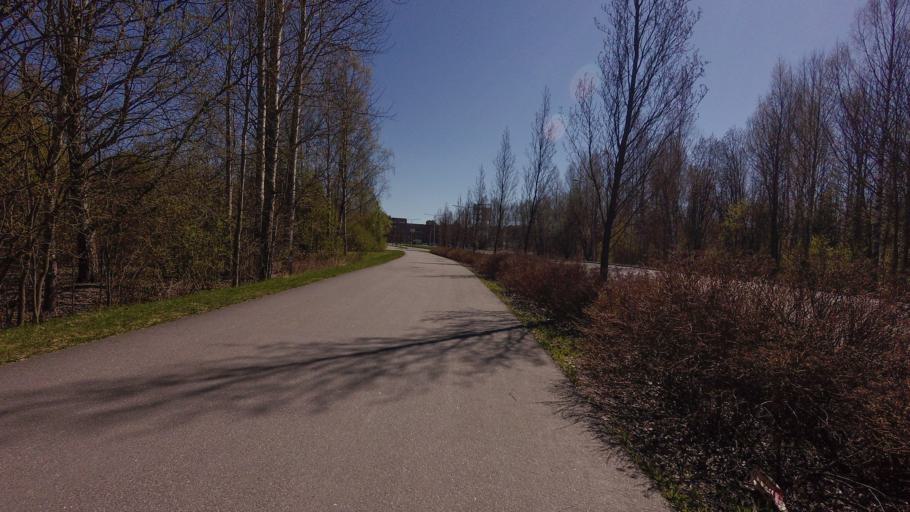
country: FI
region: Uusimaa
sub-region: Helsinki
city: Vantaa
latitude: 60.2298
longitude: 25.1215
